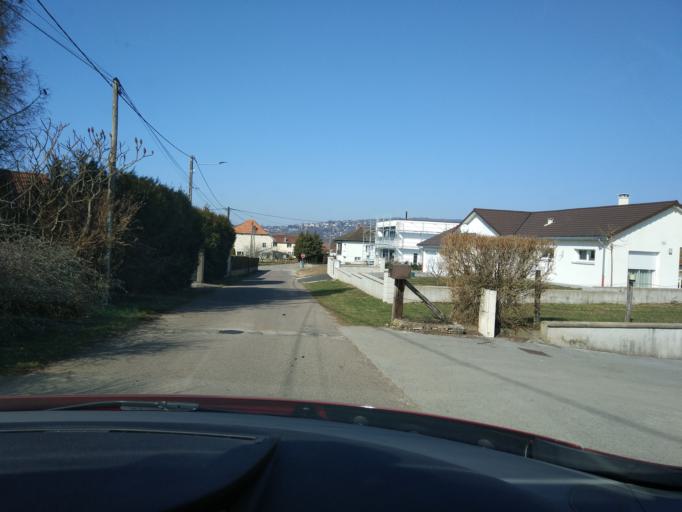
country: FR
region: Franche-Comte
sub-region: Departement du Doubs
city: Saone
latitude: 47.2156
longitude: 6.1129
